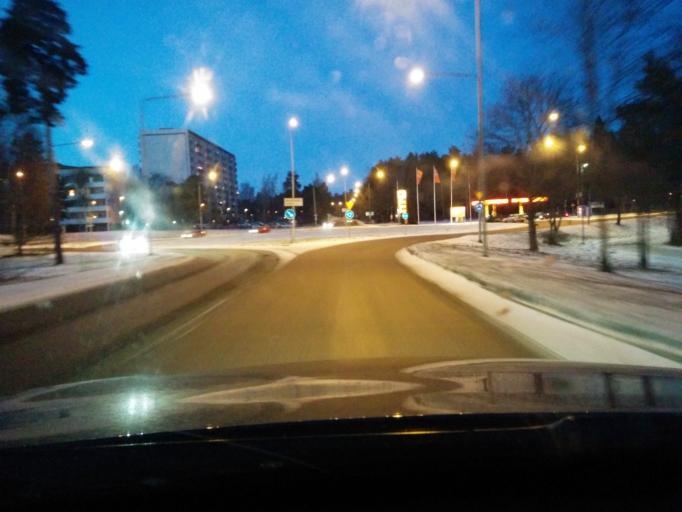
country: SE
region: Vaestmanland
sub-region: Vasteras
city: Vasteras
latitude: 59.6215
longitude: 16.5994
